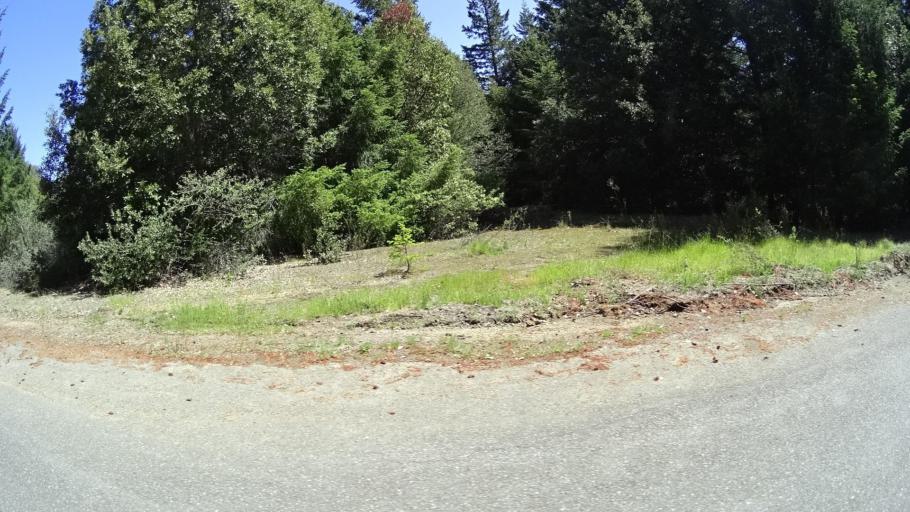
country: US
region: California
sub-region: Humboldt County
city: Redway
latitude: 40.1551
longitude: -124.0456
